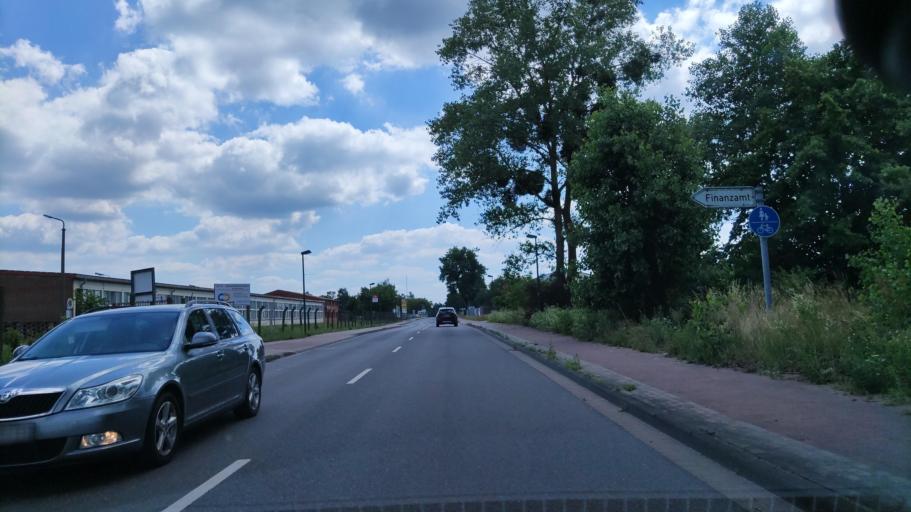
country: DE
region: Mecklenburg-Vorpommern
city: Hagenow
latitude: 53.4220
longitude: 11.1869
